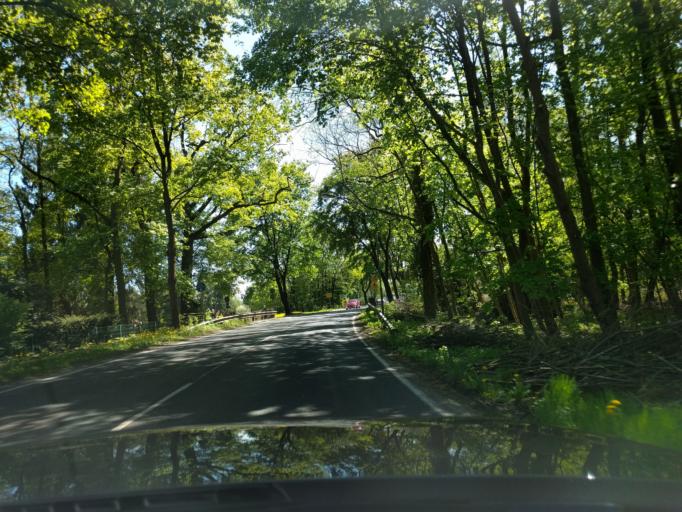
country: DE
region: Lower Saxony
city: Seevetal
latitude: 53.3970
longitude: 10.0107
